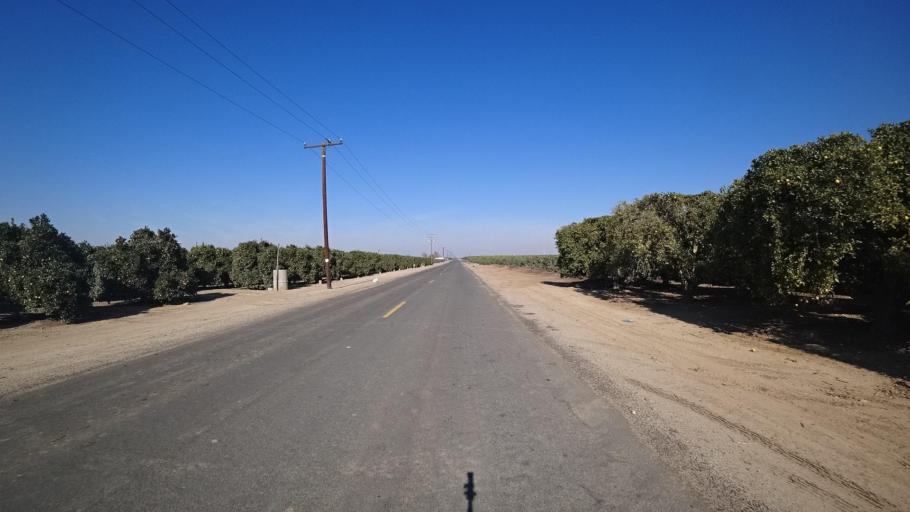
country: US
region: California
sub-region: Tulare County
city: Richgrove
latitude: 35.7196
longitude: -119.1337
